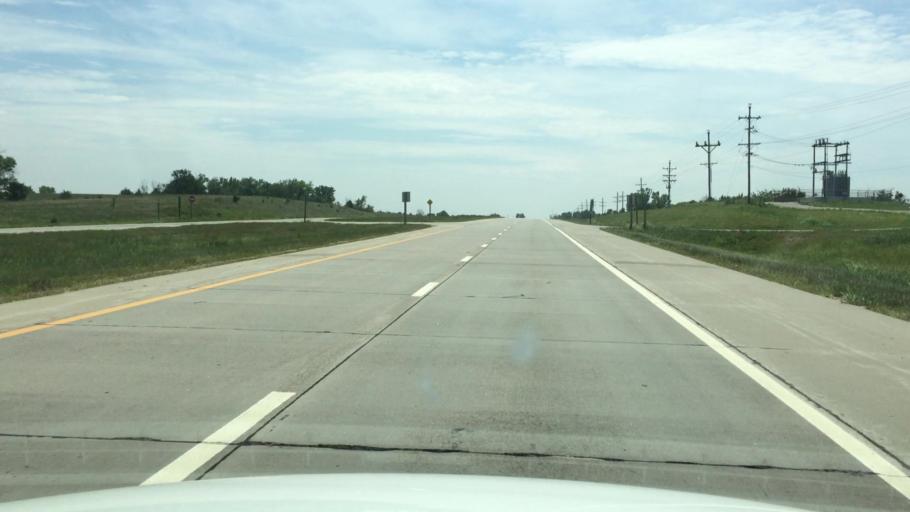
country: US
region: Kansas
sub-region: Jackson County
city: Holton
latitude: 39.2971
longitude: -95.7195
